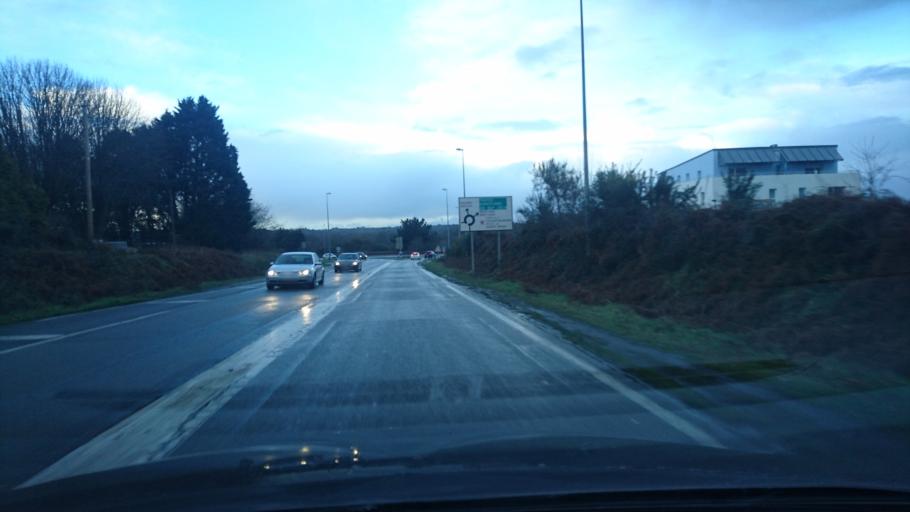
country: FR
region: Brittany
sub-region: Departement du Finistere
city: Guilers
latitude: 48.3937
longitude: -4.5392
